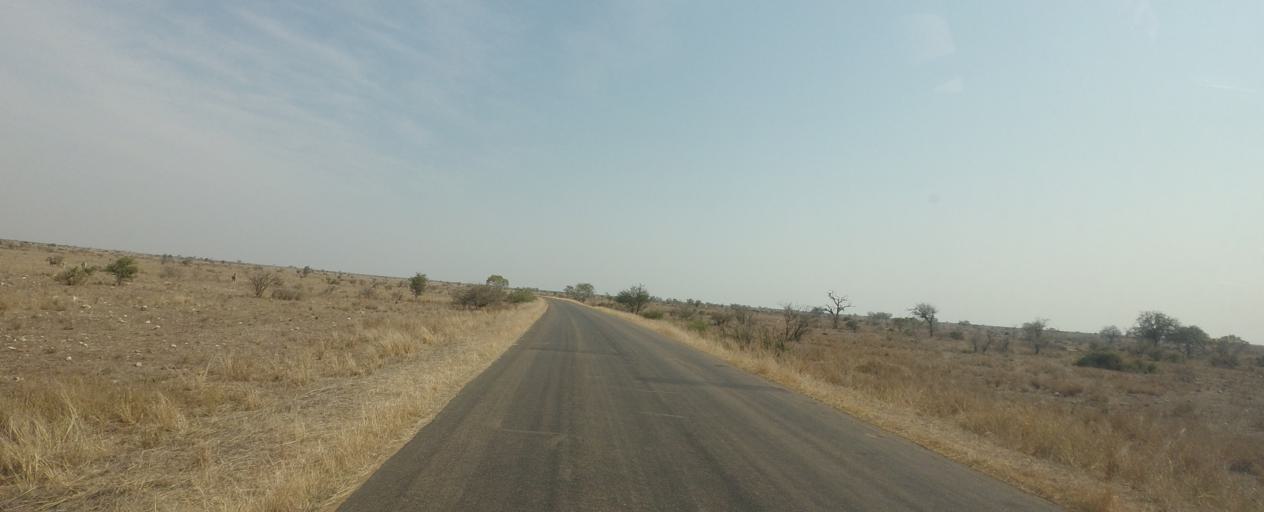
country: ZA
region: Limpopo
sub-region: Mopani District Municipality
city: Phalaborwa
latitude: -24.2793
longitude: 31.7395
